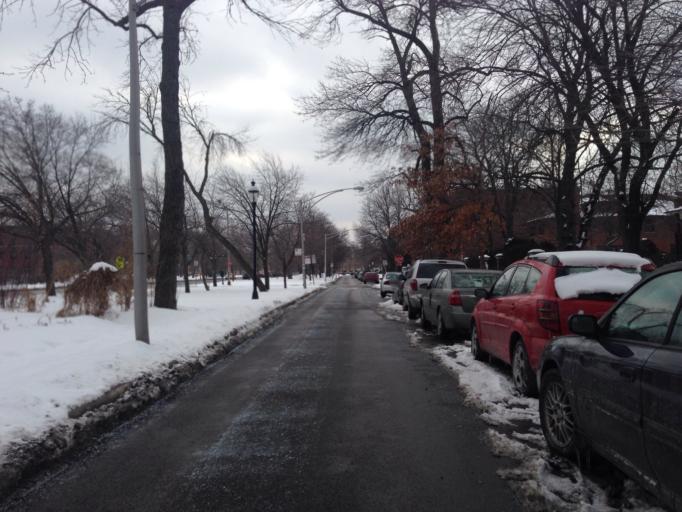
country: US
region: Illinois
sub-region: Cook County
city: Lincolnwood
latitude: 41.9236
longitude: -87.7075
